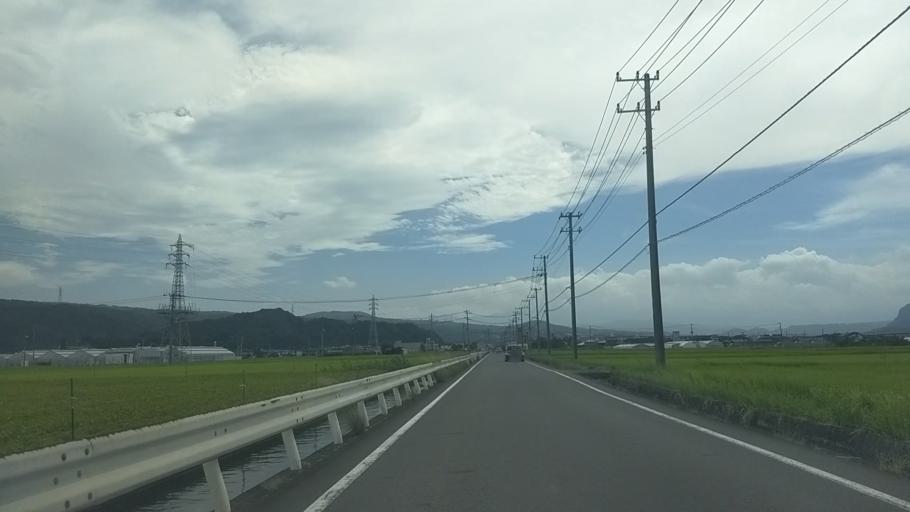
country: JP
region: Shizuoka
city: Mishima
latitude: 35.0641
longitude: 138.9466
